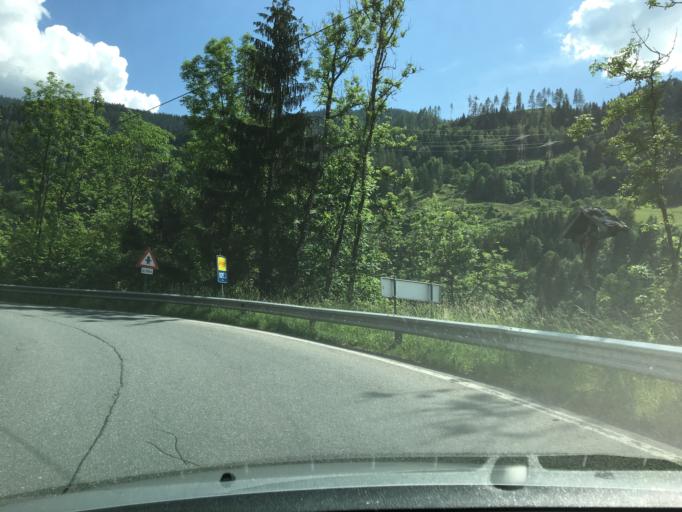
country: AT
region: Salzburg
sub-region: Politischer Bezirk Sankt Johann im Pongau
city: Sankt Johann im Pongau
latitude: 47.3347
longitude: 13.2182
